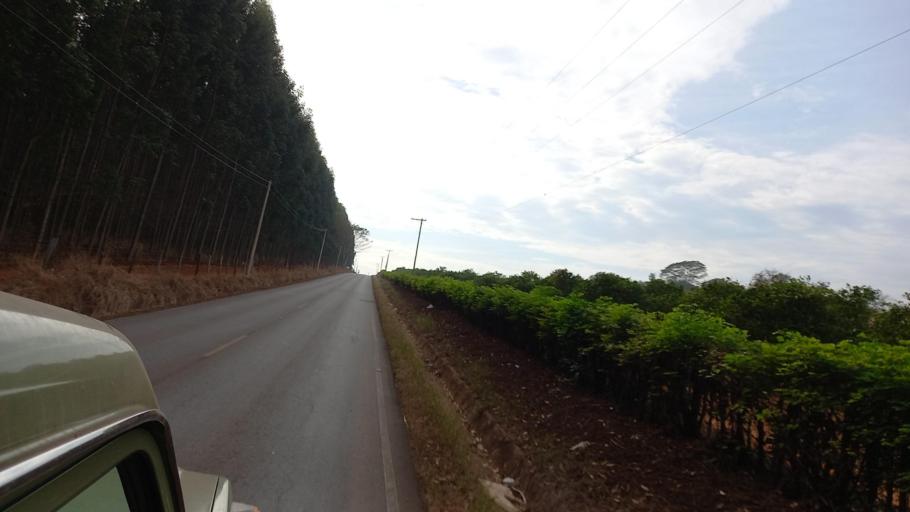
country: BR
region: Sao Paulo
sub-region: Moji-Guacu
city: Mogi-Gaucu
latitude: -22.3308
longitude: -46.8740
